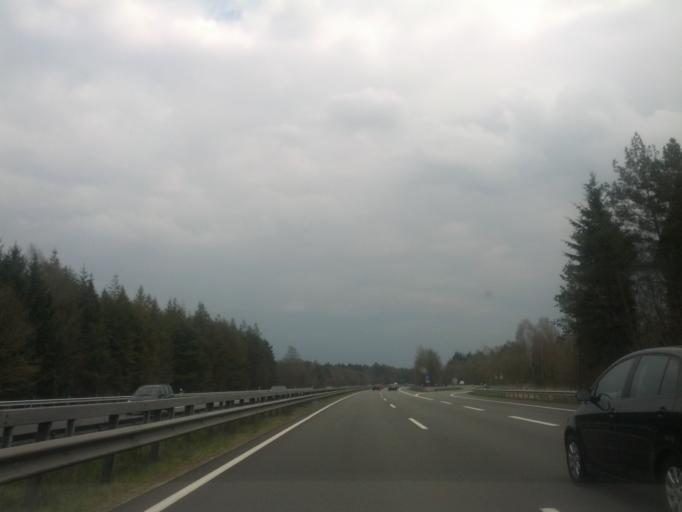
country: DE
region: Lower Saxony
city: Bad Zwischenahn
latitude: 53.2490
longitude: 8.0018
